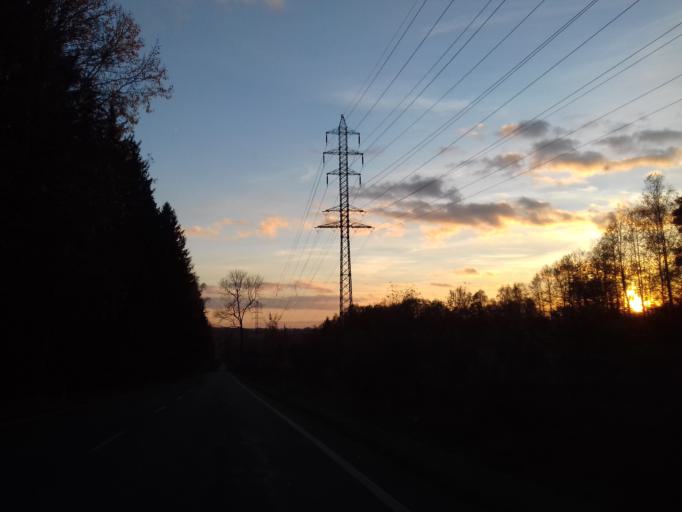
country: CZ
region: Pardubicky
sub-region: Okres Chrudim
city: Hlinsko
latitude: 49.7359
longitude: 15.8763
